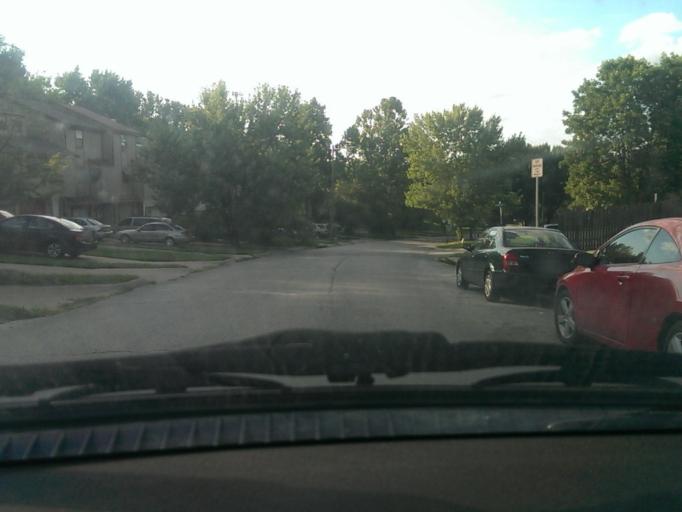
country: US
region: Kansas
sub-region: Johnson County
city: Westwood
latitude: 39.0673
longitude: -94.6095
